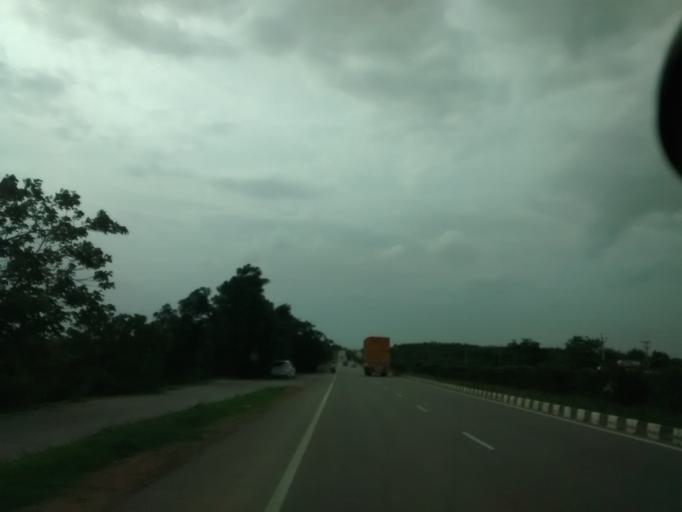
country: IN
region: Telangana
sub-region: Mahbubnagar
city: Gadwal
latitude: 16.0502
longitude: 77.9163
